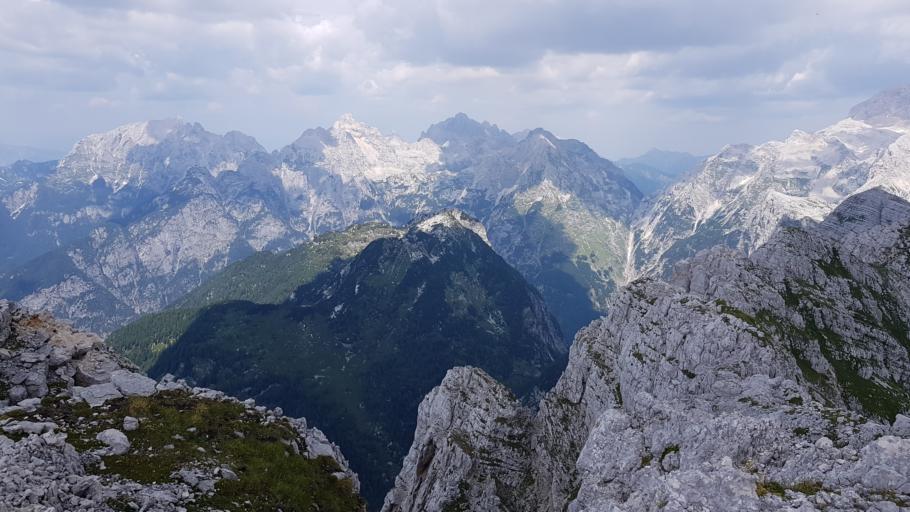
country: SI
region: Kranjska Gora
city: Kranjska Gora
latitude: 46.3437
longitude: 13.7672
